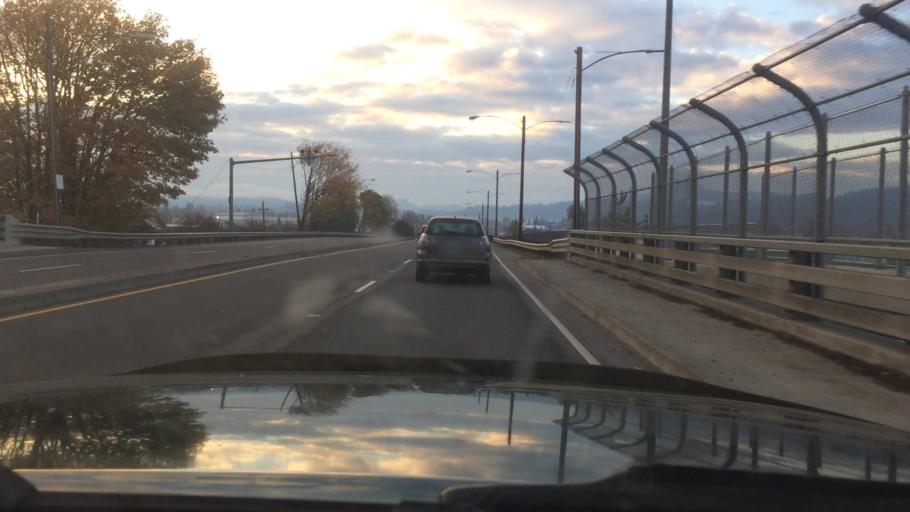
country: US
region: Oregon
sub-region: Lane County
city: Eugene
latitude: 44.0604
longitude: -123.1338
